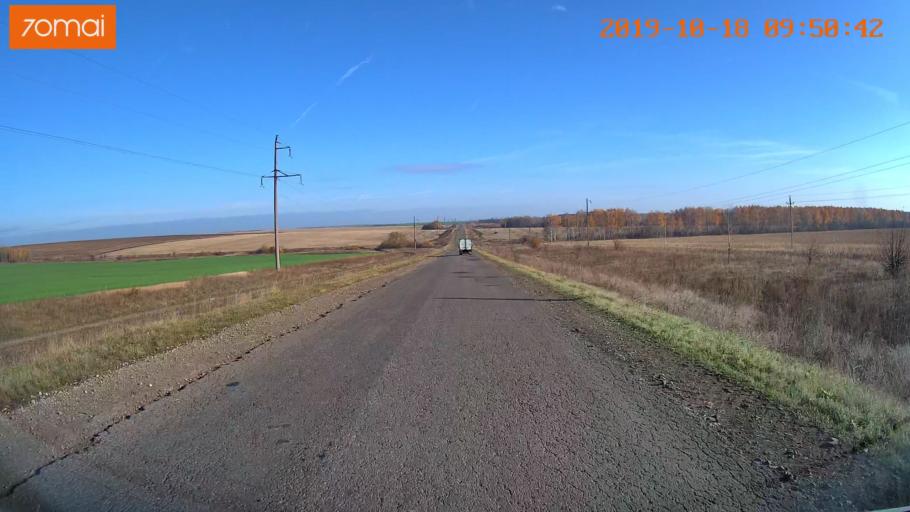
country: RU
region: Tula
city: Kazachka
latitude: 53.3317
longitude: 38.2812
